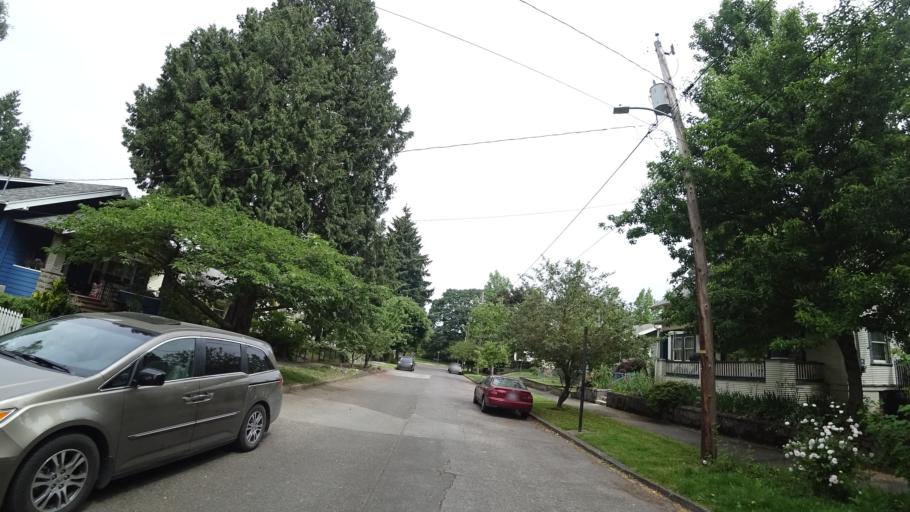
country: US
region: Oregon
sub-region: Multnomah County
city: Portland
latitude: 45.5674
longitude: -122.6371
